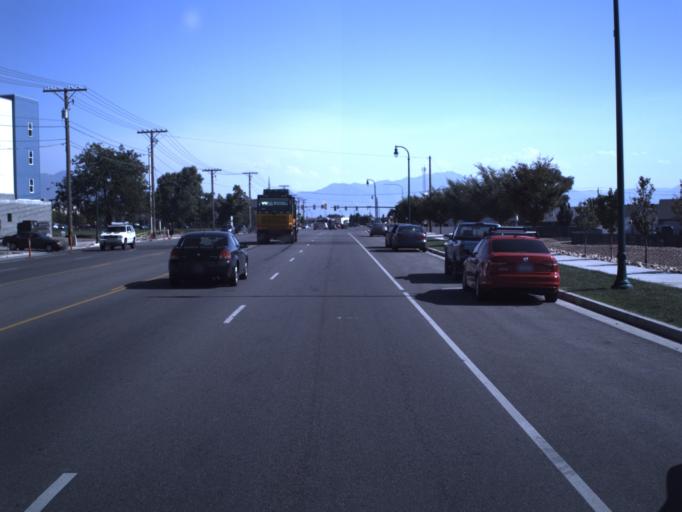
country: US
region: Utah
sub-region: Utah County
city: Orem
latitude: 40.2814
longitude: -111.7316
